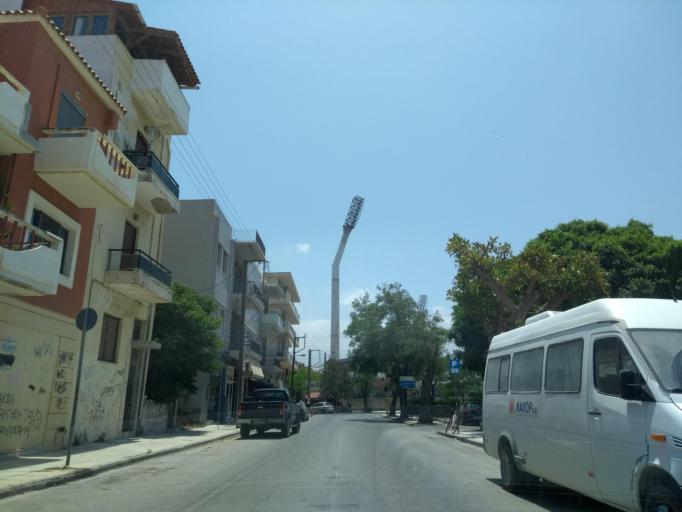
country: GR
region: Crete
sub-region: Nomos Chanias
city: Chania
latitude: 35.5151
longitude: 24.0253
